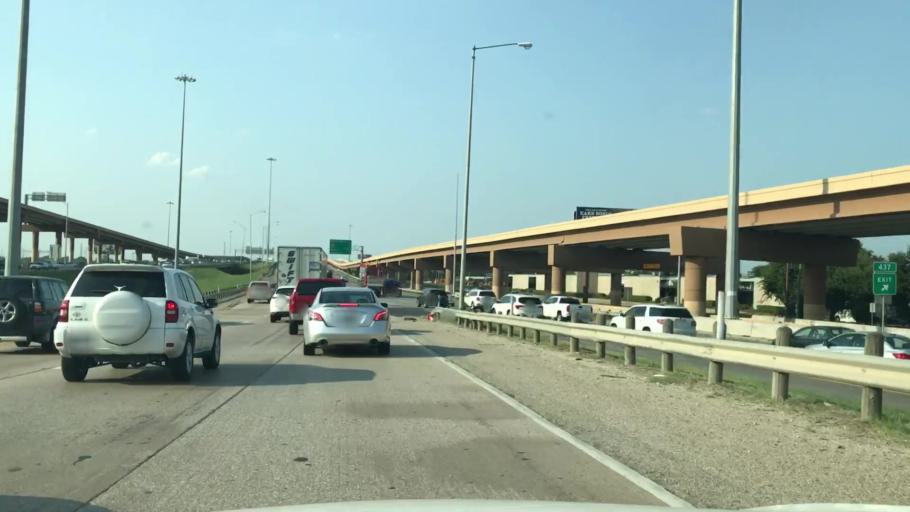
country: US
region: Texas
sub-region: Dallas County
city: Farmers Branch
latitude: 32.8710
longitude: -96.8971
